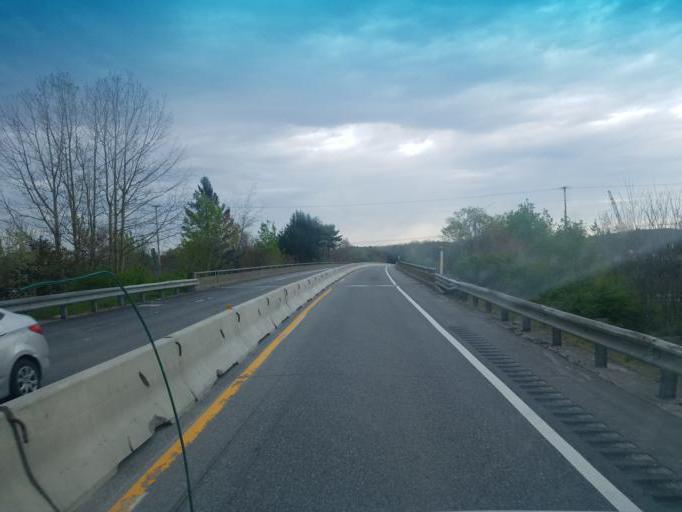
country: US
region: Maine
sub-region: Somerset County
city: Pittsfield
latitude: 44.7998
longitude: -69.3946
